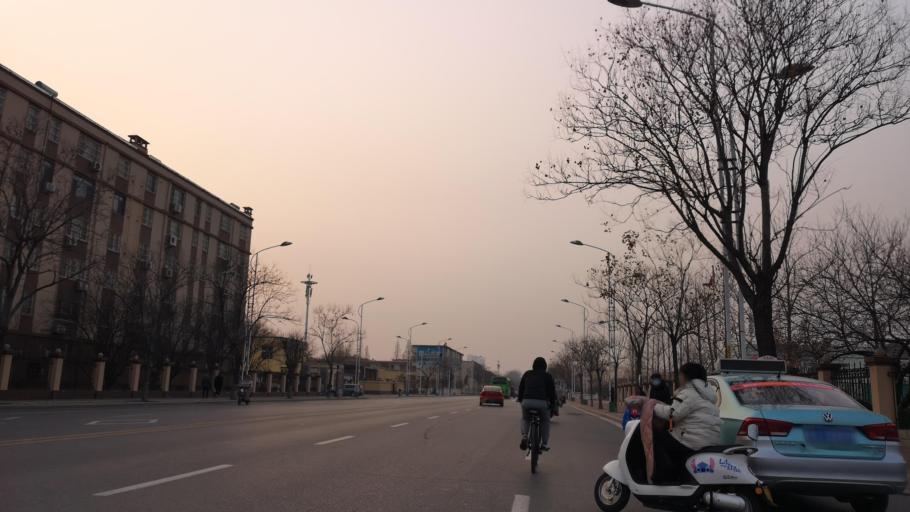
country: CN
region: Henan Sheng
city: Zhongyuanlu
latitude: 35.7840
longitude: 115.0787
